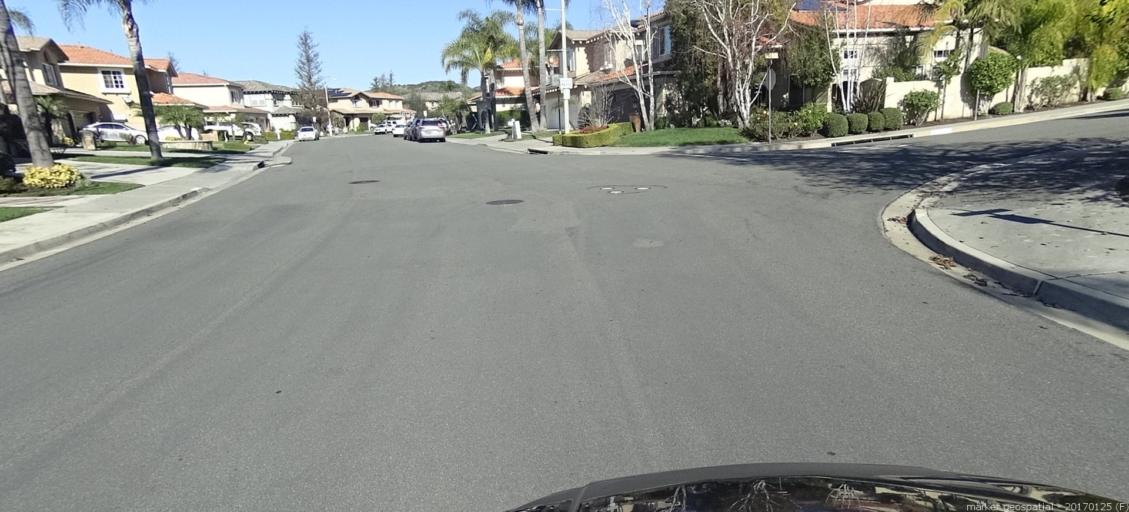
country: US
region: California
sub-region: Orange County
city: Portola Hills
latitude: 33.6802
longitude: -117.6367
